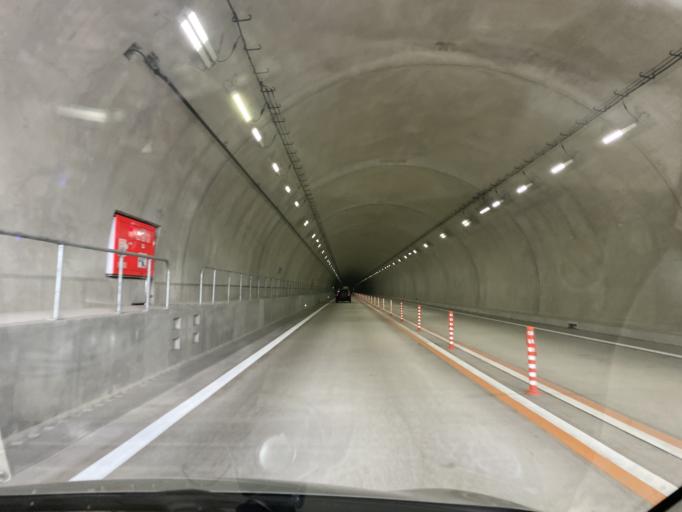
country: JP
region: Hyogo
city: Toyooka
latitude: 35.4992
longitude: 134.7907
